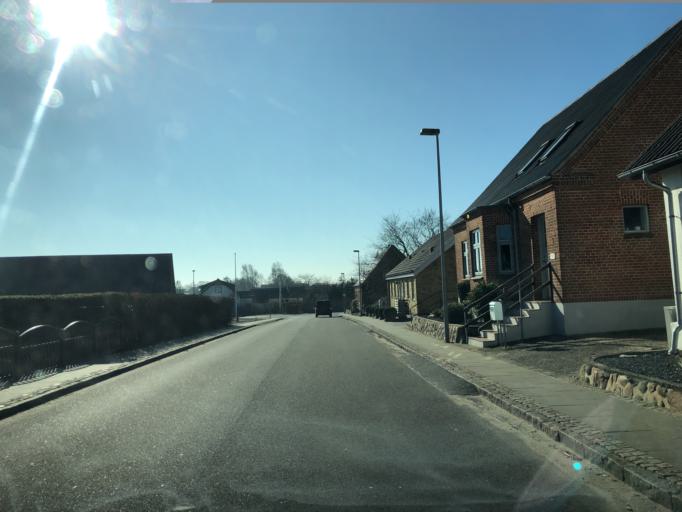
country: DK
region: Central Jutland
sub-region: Ikast-Brande Kommune
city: Bording Kirkeby
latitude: 56.1479
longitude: 9.2771
